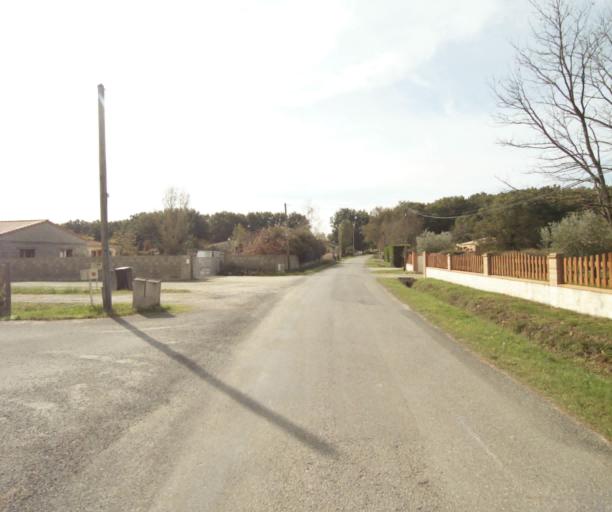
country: FR
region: Midi-Pyrenees
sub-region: Departement du Tarn-et-Garonne
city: Orgueil
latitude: 43.8930
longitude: 1.4055
